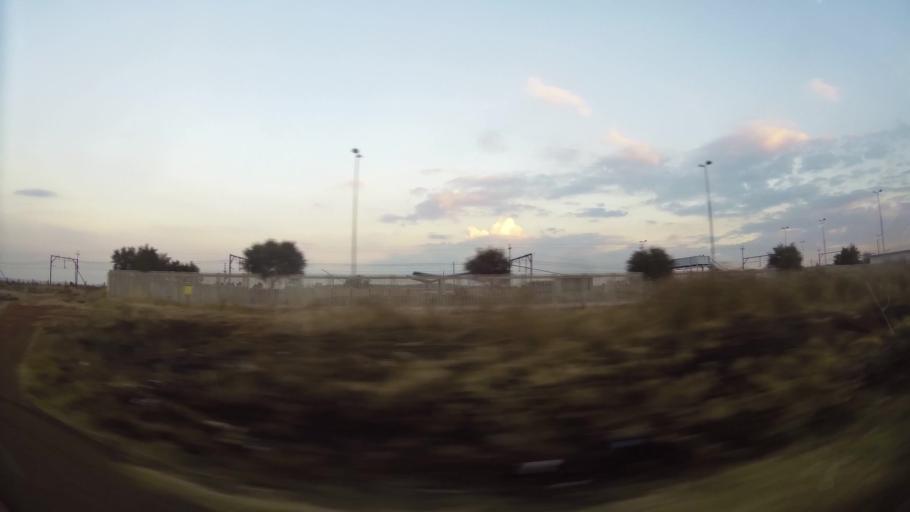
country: ZA
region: Gauteng
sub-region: City of Johannesburg Metropolitan Municipality
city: Orange Farm
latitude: -26.5652
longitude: 27.8639
